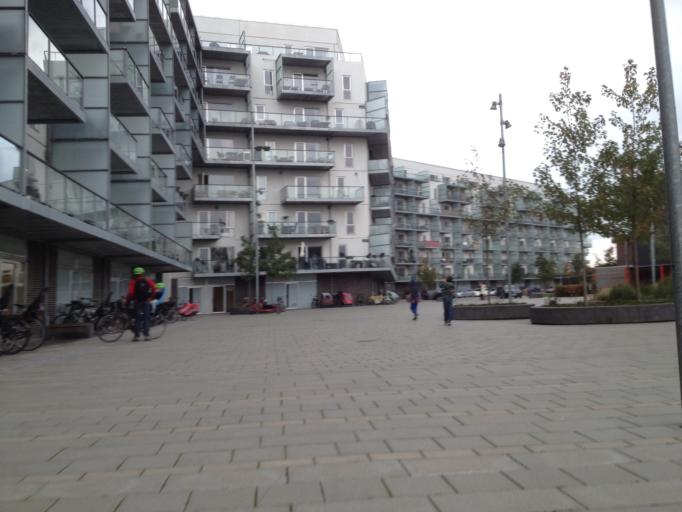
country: DK
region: Capital Region
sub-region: Kobenhavn
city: Christianshavn
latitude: 55.6866
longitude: 12.6153
